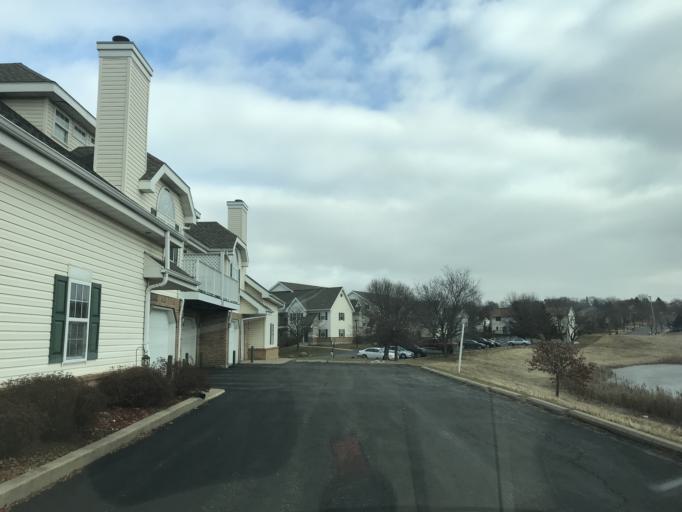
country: US
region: Wisconsin
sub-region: Dane County
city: Monona
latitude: 43.1072
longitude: -89.2989
